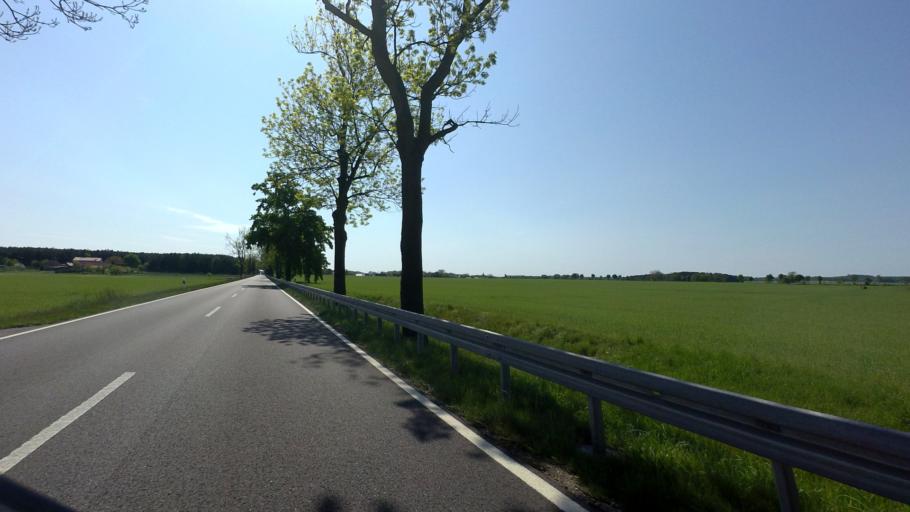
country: DE
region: Brandenburg
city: Neu Zauche
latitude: 52.0334
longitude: 14.0976
